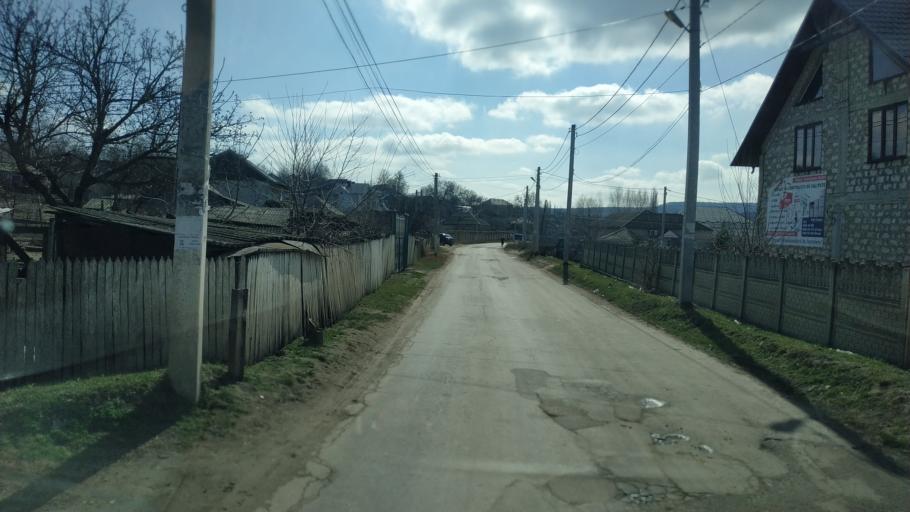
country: MD
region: Straseni
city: Straseni
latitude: 47.0131
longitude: 28.5440
